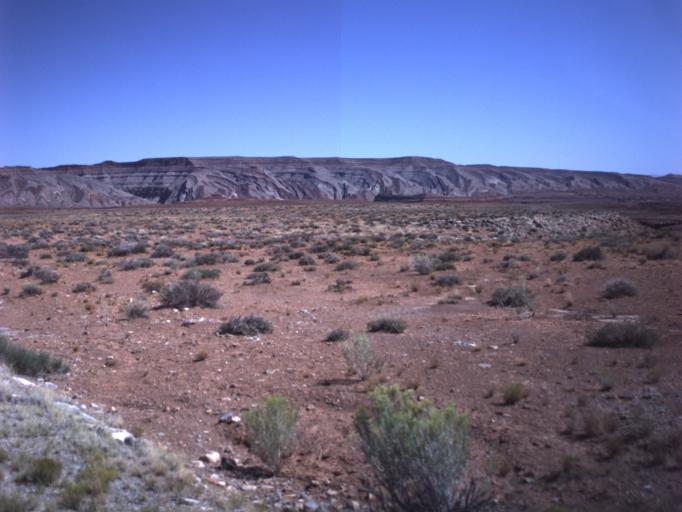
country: US
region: Arizona
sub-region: Navajo County
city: Kayenta
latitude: 37.2002
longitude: -109.8960
